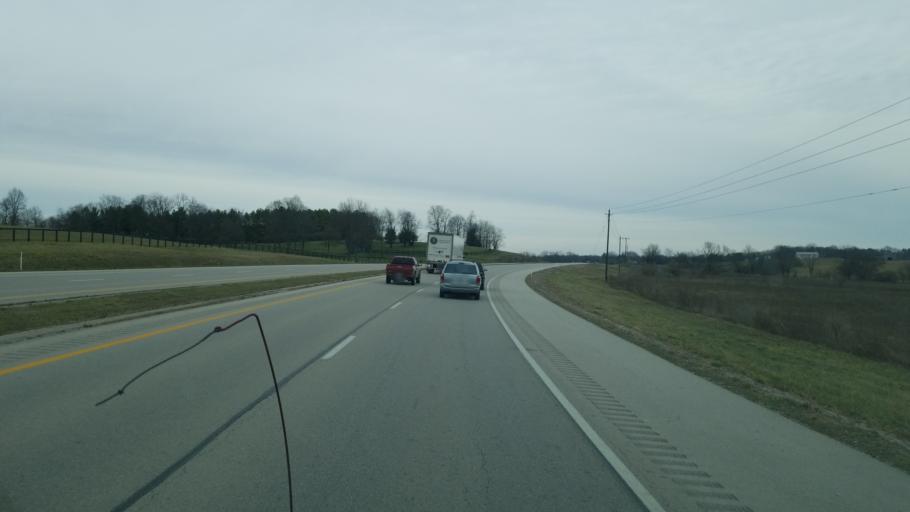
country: US
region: Kentucky
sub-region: Bourbon County
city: Paris
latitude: 38.2257
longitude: -84.2712
